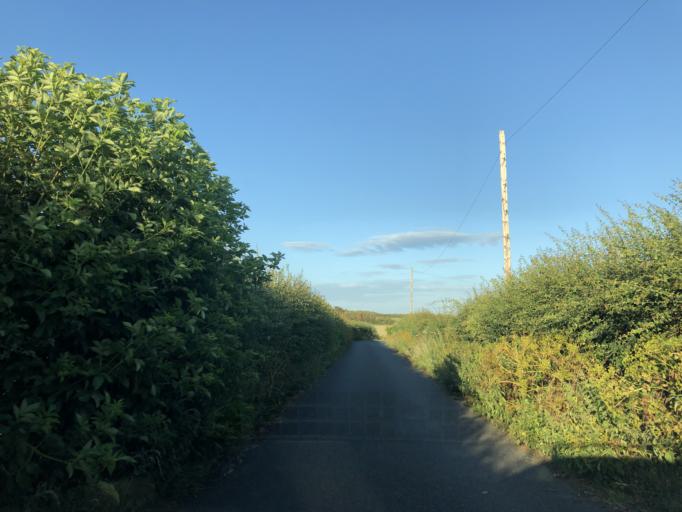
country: GB
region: England
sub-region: Isle of Wight
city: Chale
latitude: 50.6317
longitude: -1.3787
